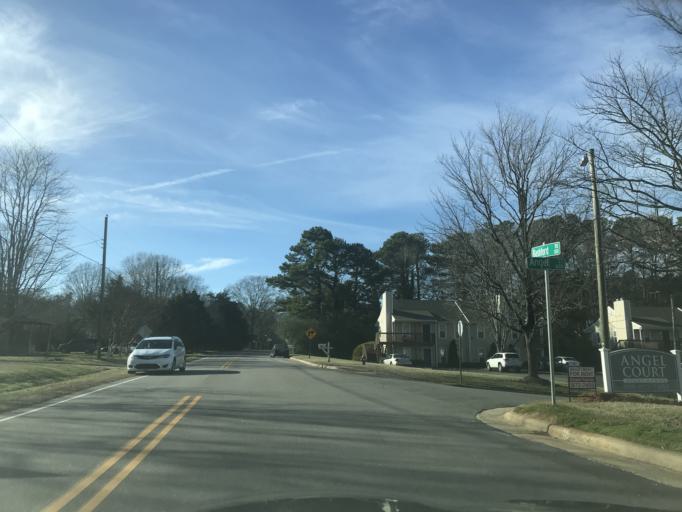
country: US
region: North Carolina
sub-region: Wake County
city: Cary
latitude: 35.7853
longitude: -78.7412
